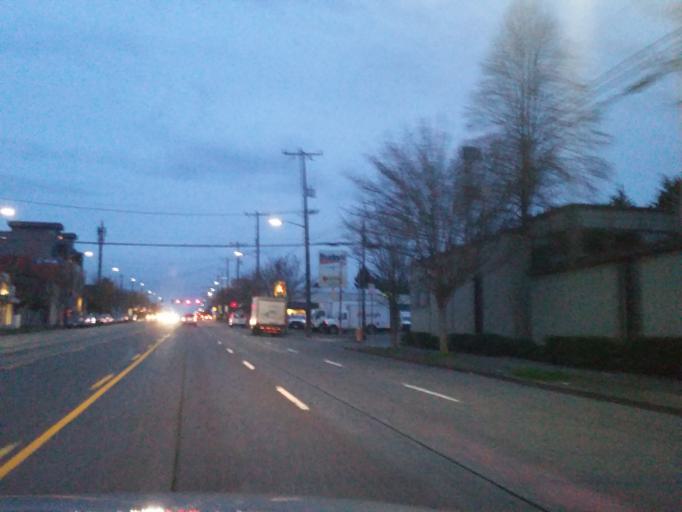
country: US
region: Washington
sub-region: King County
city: Shoreline
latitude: 47.6846
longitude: -122.3768
